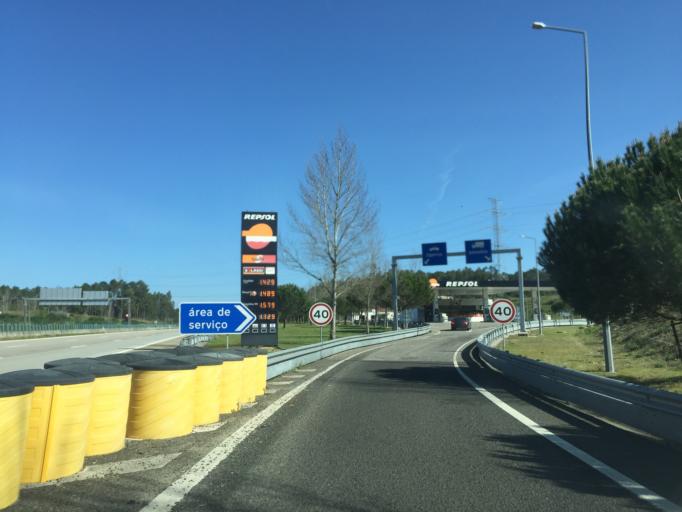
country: PT
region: Leiria
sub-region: Leiria
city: Monte Redondo
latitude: 39.9069
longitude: -8.8023
